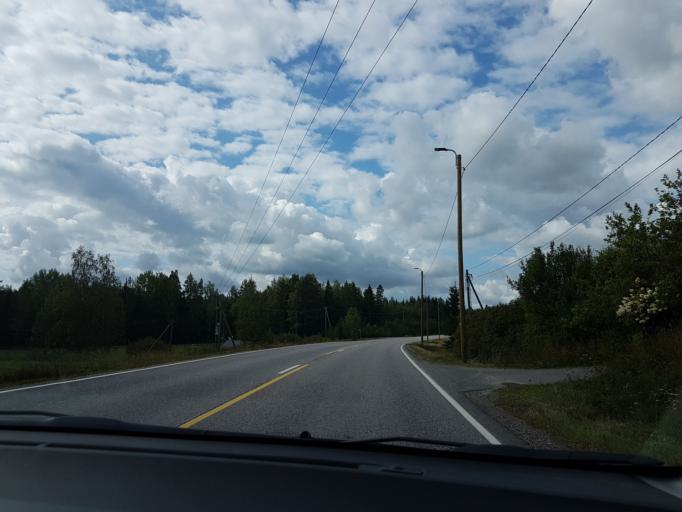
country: FI
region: Uusimaa
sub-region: Helsinki
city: Pornainen
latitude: 60.4805
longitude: 25.3388
